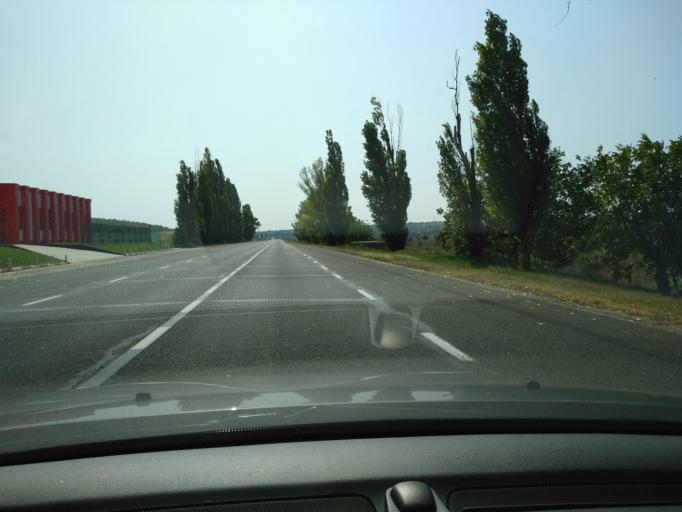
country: RO
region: Vaslui
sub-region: Comuna Dranceni
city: Dranceni
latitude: 46.8413
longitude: 28.2028
